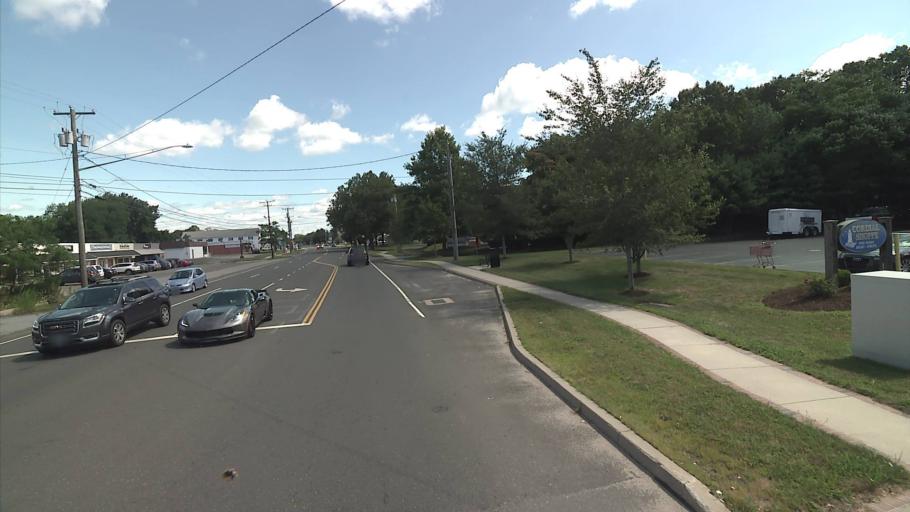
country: US
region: Connecticut
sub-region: Middlesex County
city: Old Saybrook
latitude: 41.2902
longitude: -72.3857
